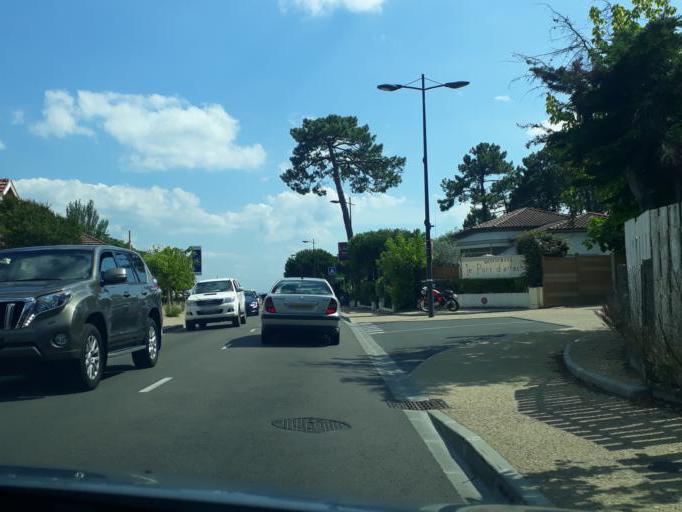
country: FR
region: Aquitaine
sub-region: Departement de la Gironde
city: Ares
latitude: 44.7454
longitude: -1.1814
